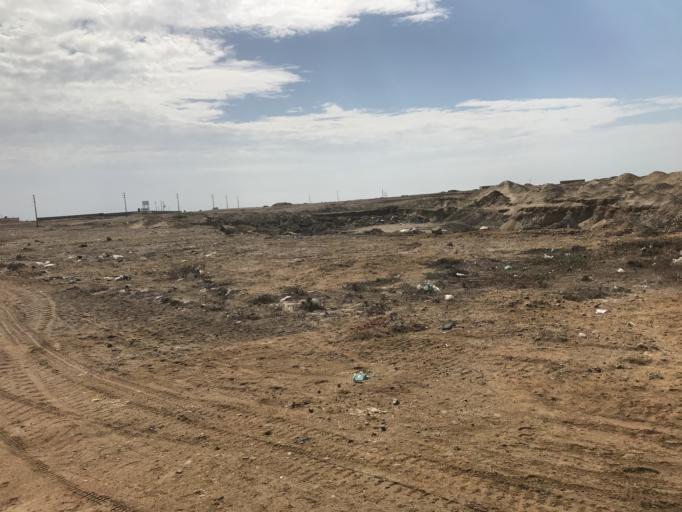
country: PE
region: Lambayeque
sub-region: Provincia de Chiclayo
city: Eten
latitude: -6.8998
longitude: -79.8428
